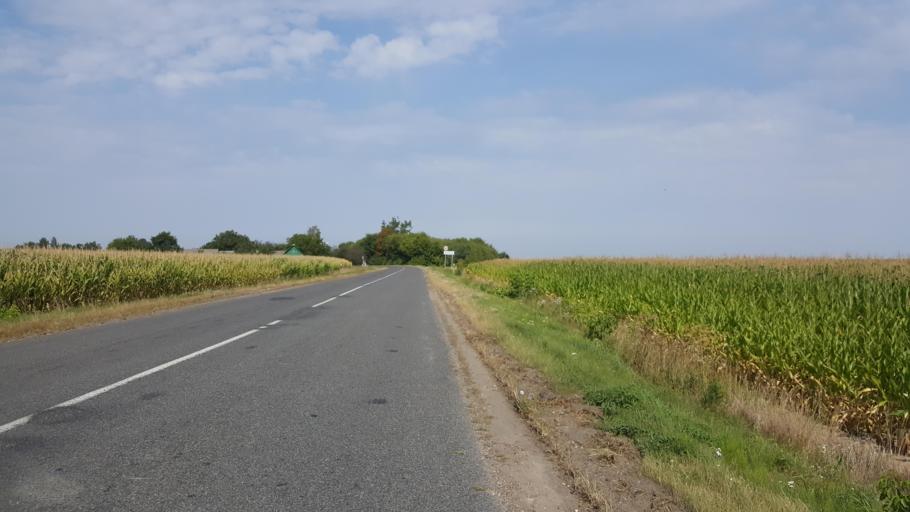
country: BY
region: Brest
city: Kamyanyets
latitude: 52.4234
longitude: 23.7724
